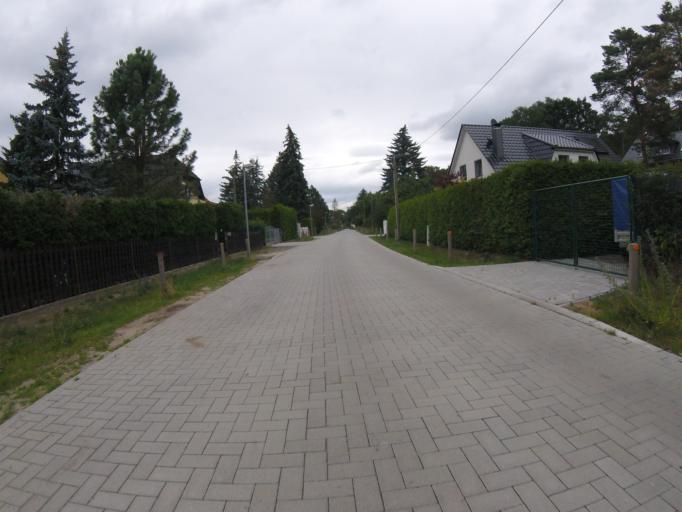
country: DE
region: Brandenburg
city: Konigs Wusterhausen
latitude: 52.2837
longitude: 13.6569
